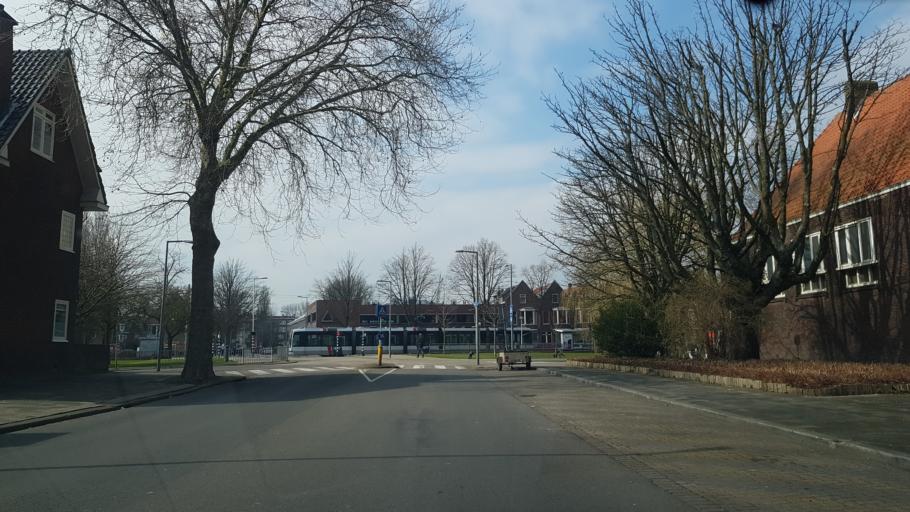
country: NL
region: South Holland
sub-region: Gemeente Rotterdam
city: Delfshaven
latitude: 51.8869
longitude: 4.4667
